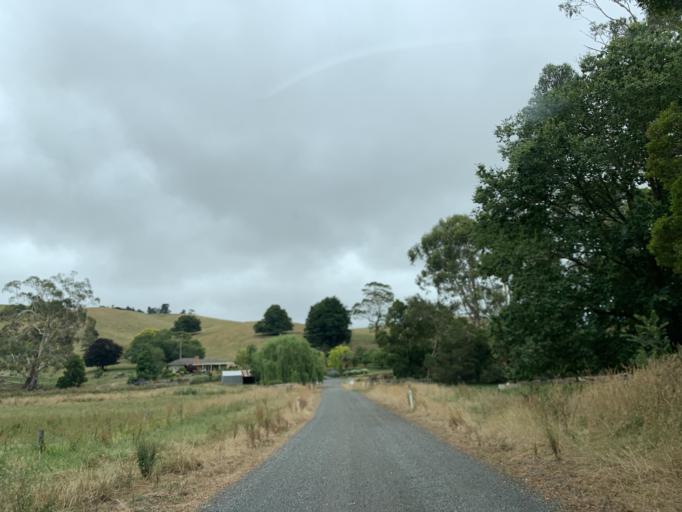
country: AU
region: Victoria
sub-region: Baw Baw
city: Warragul
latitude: -38.3212
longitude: 145.8330
